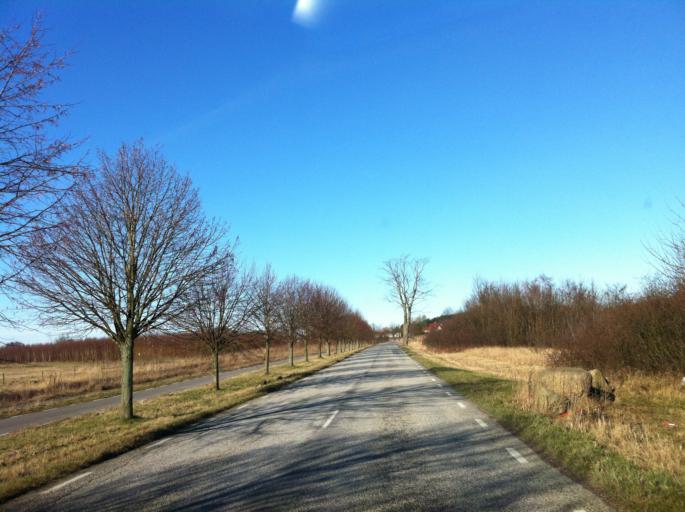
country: SE
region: Skane
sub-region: Svedala Kommun
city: Klagerup
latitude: 55.5699
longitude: 13.2021
